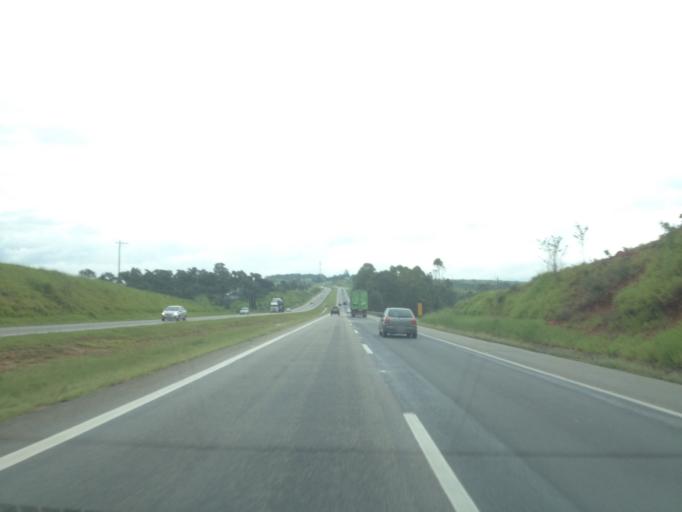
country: BR
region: Sao Paulo
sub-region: Itu
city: Itu
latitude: -23.3465
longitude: -47.3249
